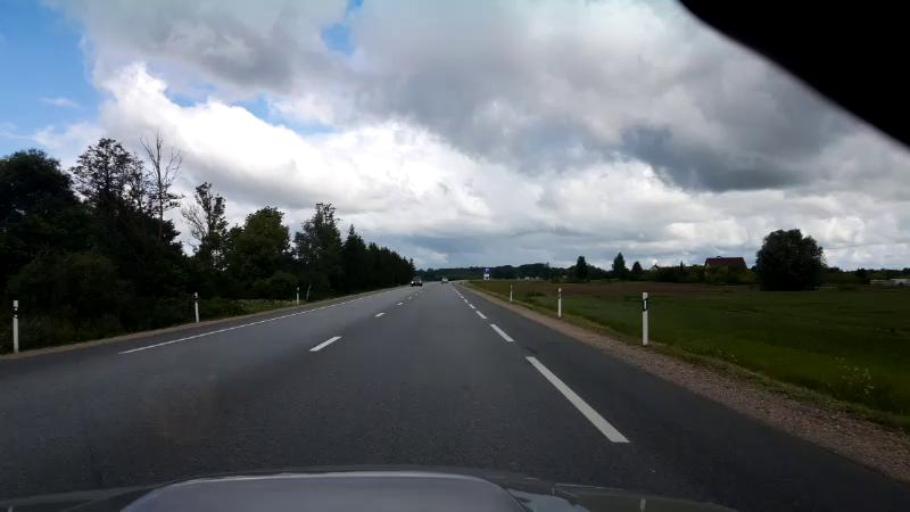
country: LV
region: Bauskas Rajons
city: Bauska
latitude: 56.4431
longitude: 24.1678
